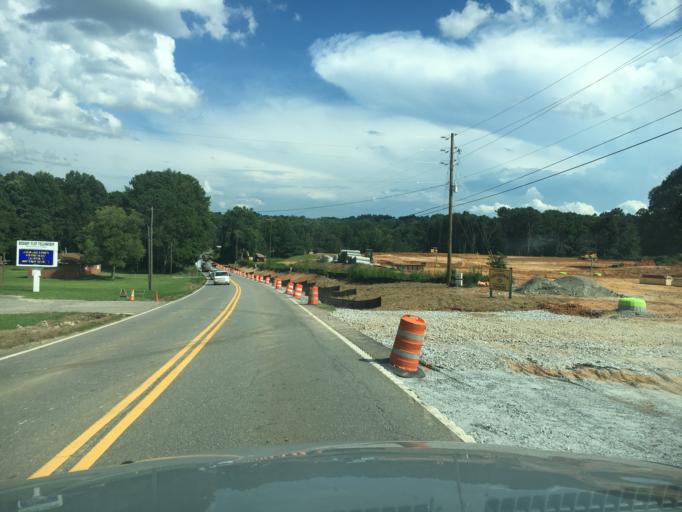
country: US
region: Georgia
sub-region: Cherokee County
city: Holly Springs
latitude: 34.1811
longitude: -84.4339
